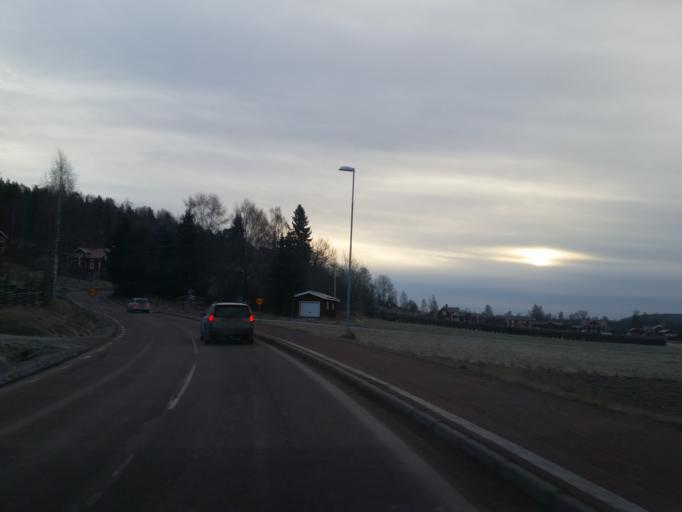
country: SE
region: Dalarna
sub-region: Leksand Municipality
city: Leksand
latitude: 60.7304
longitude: 15.0272
